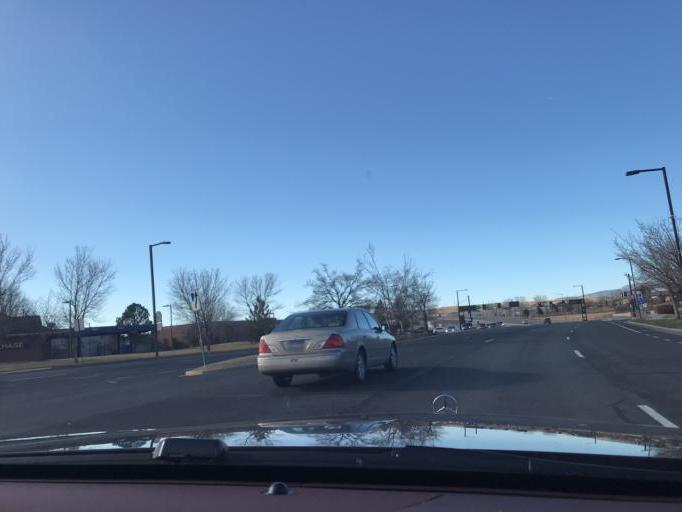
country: US
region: Colorado
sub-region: Boulder County
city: Superior
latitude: 39.9630
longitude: -105.1637
